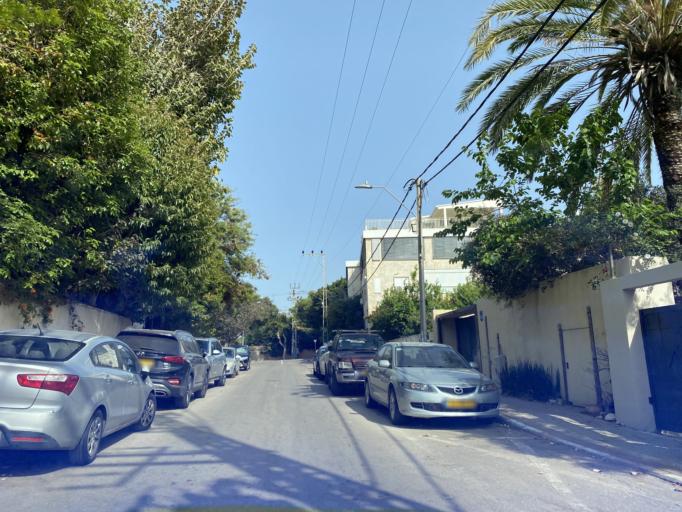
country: IL
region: Tel Aviv
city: Herzliya Pituah
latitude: 32.1740
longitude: 34.8073
